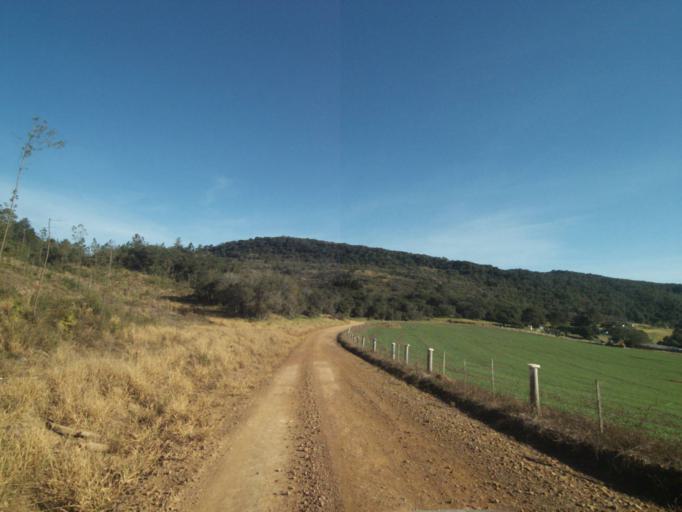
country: BR
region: Parana
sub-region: Tibagi
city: Tibagi
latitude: -24.5548
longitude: -50.5219
